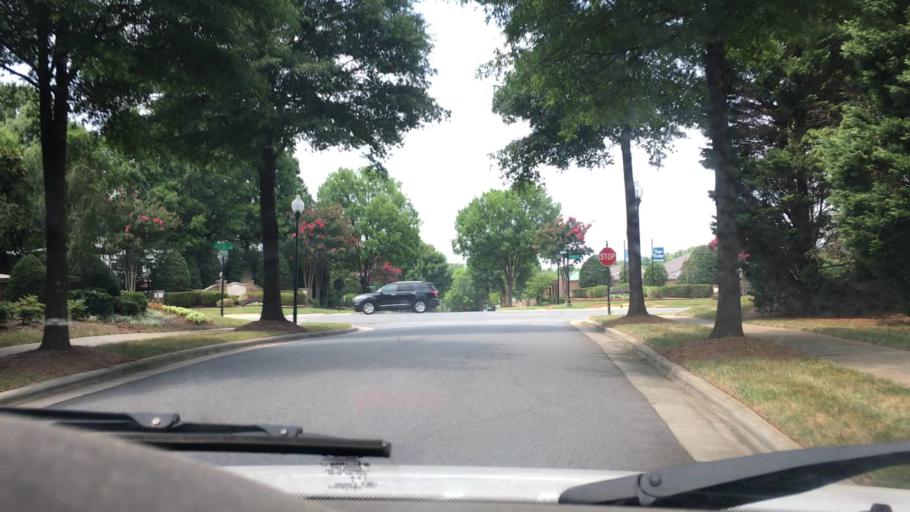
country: US
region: North Carolina
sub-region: Mecklenburg County
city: Cornelius
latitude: 35.4761
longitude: -80.8960
